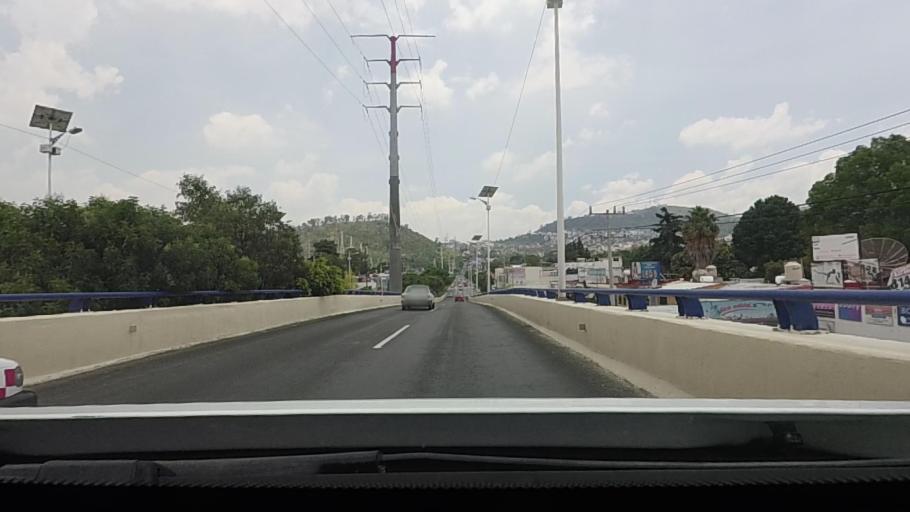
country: MX
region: Mexico
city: Naucalpan de Juarez
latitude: 19.4911
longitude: -99.2551
